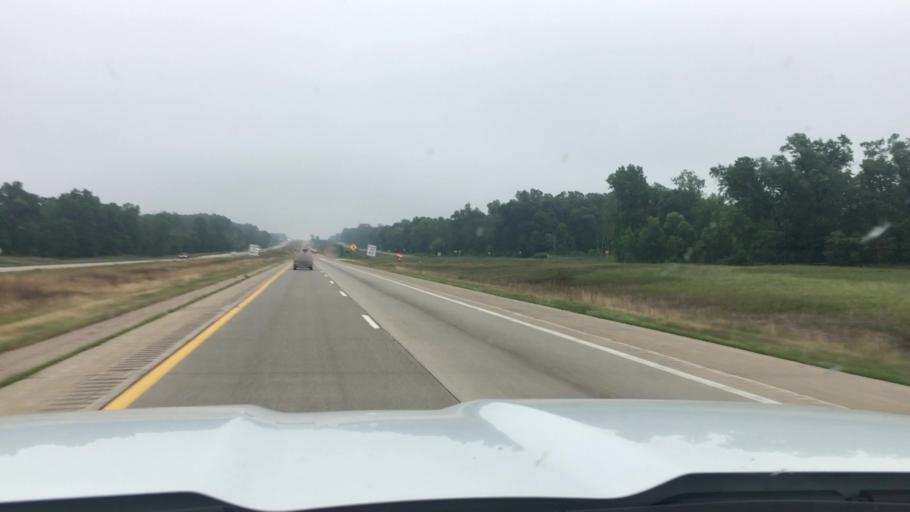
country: US
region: Michigan
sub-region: Ingham County
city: Haslett
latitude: 42.8001
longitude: -84.3474
